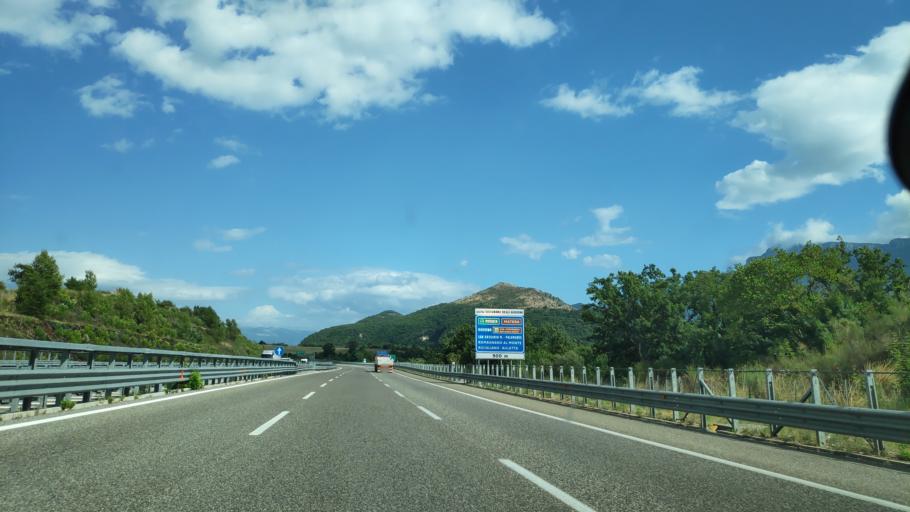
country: IT
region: Campania
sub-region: Provincia di Salerno
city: Palomonte
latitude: 40.6127
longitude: 15.2814
